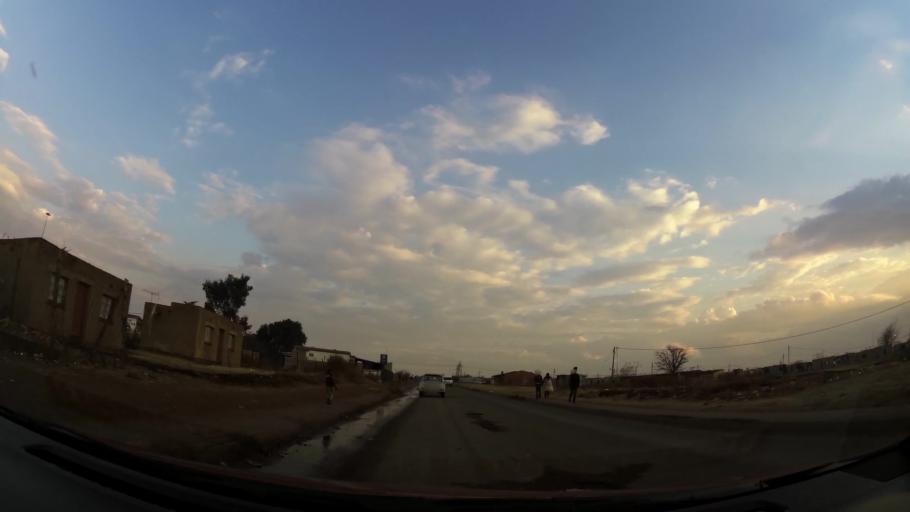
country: ZA
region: Gauteng
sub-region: City of Johannesburg Metropolitan Municipality
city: Orange Farm
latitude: -26.5511
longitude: 27.8406
